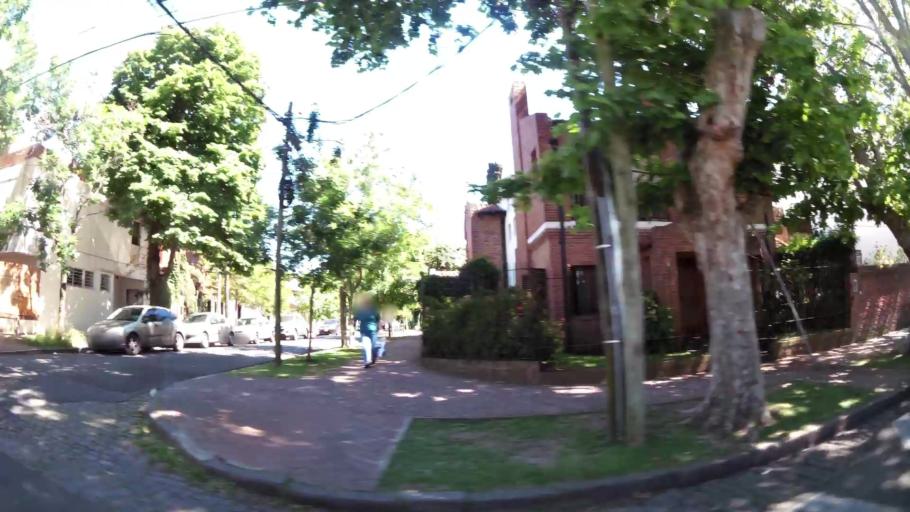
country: AR
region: Buenos Aires
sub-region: Partido de Vicente Lopez
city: Olivos
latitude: -34.5330
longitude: -58.4952
